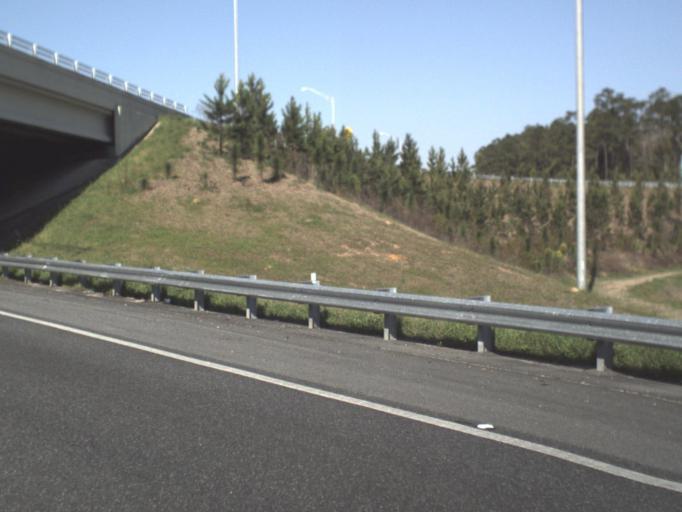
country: US
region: Florida
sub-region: Leon County
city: Tallahassee
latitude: 30.4829
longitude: -84.3087
